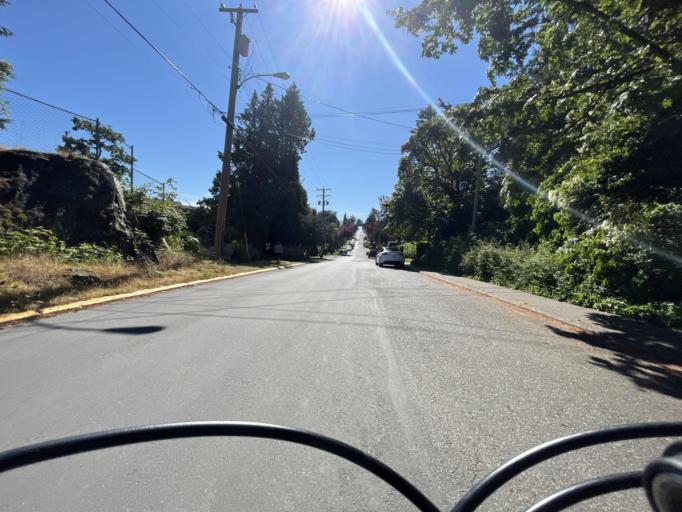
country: CA
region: British Columbia
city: Victoria
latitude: 48.4429
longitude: -123.4000
